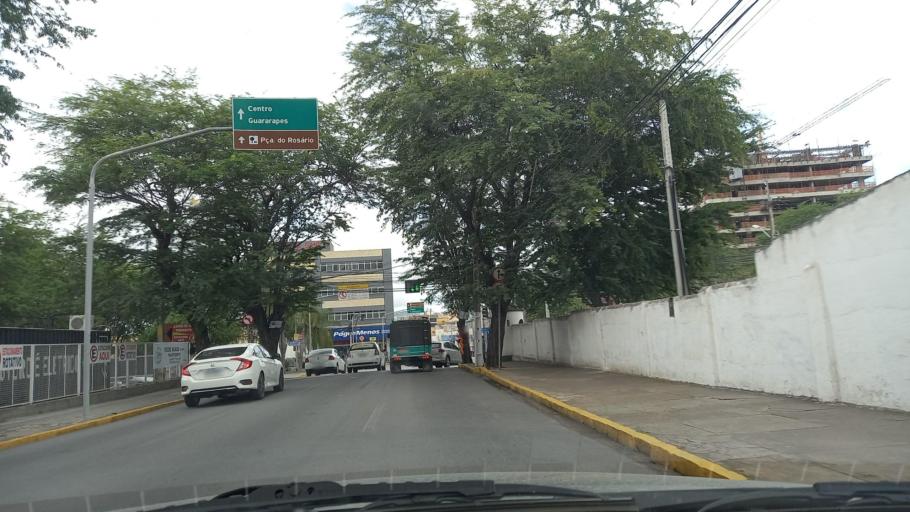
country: BR
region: Pernambuco
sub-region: Caruaru
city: Caruaru
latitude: -8.2825
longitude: -35.9680
